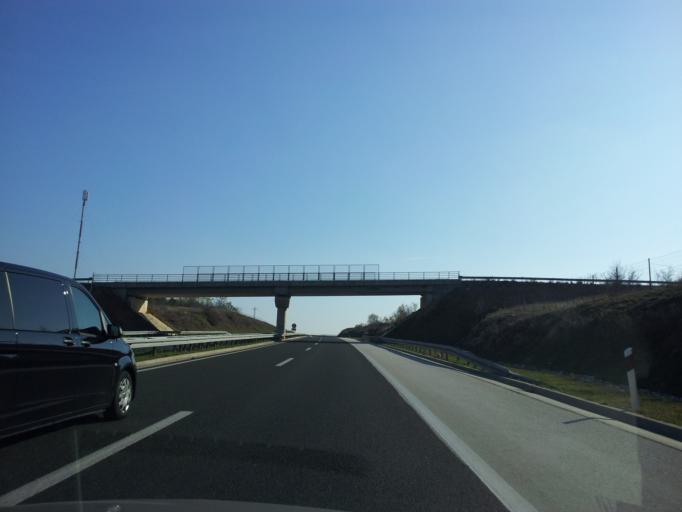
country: HR
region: Zadarska
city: Posedarje
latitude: 44.2080
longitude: 15.4451
